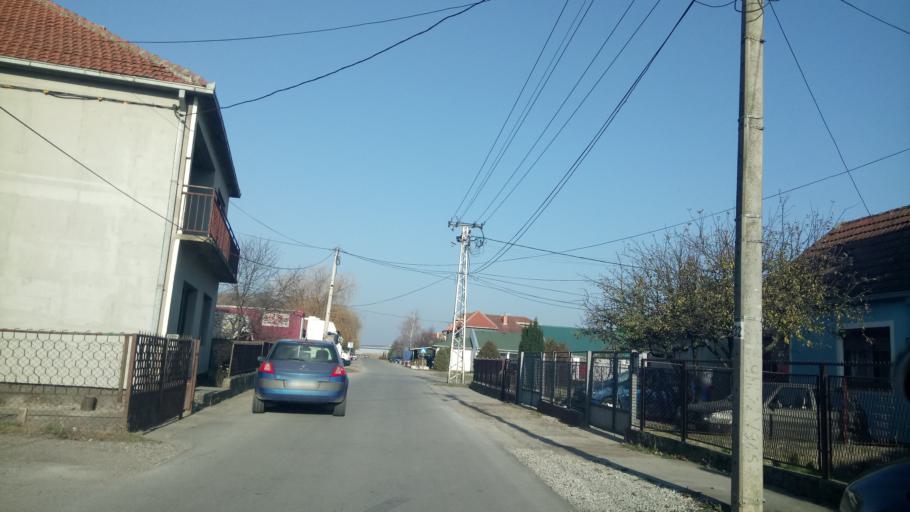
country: RS
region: Autonomna Pokrajina Vojvodina
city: Nova Pazova
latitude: 44.9470
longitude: 20.2039
